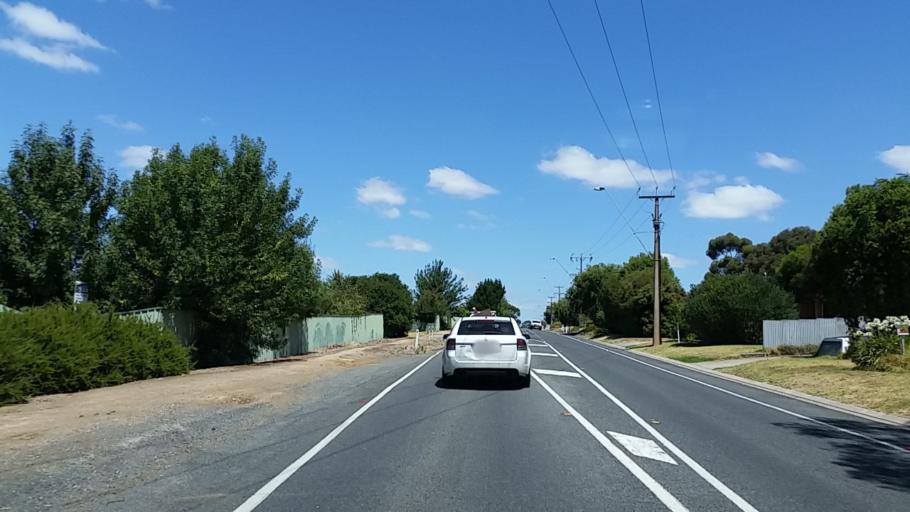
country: AU
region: South Australia
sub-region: Mount Barker
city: Nairne
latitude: -35.0262
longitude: 138.9019
